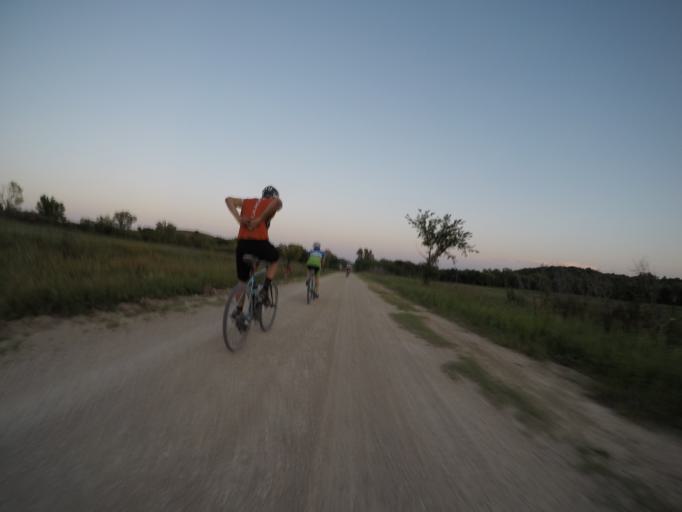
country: US
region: Kansas
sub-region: Riley County
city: Ogden
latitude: 38.9923
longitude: -96.5654
